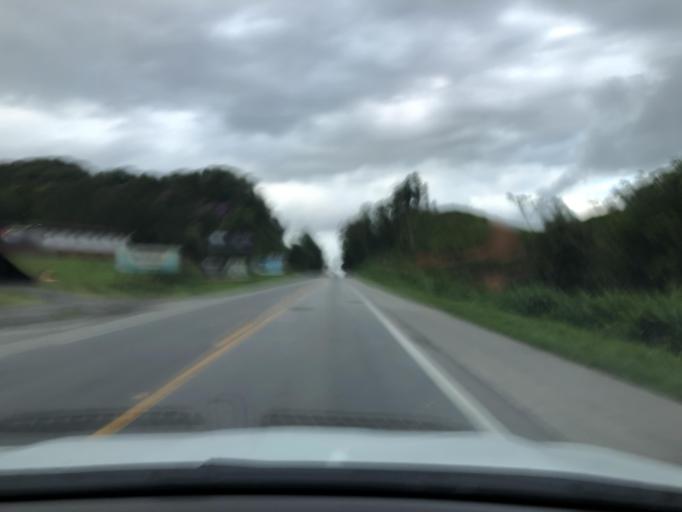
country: BR
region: Santa Catarina
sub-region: Sao Francisco Do Sul
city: Sao Francisco do Sul
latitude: -26.3127
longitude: -48.6442
